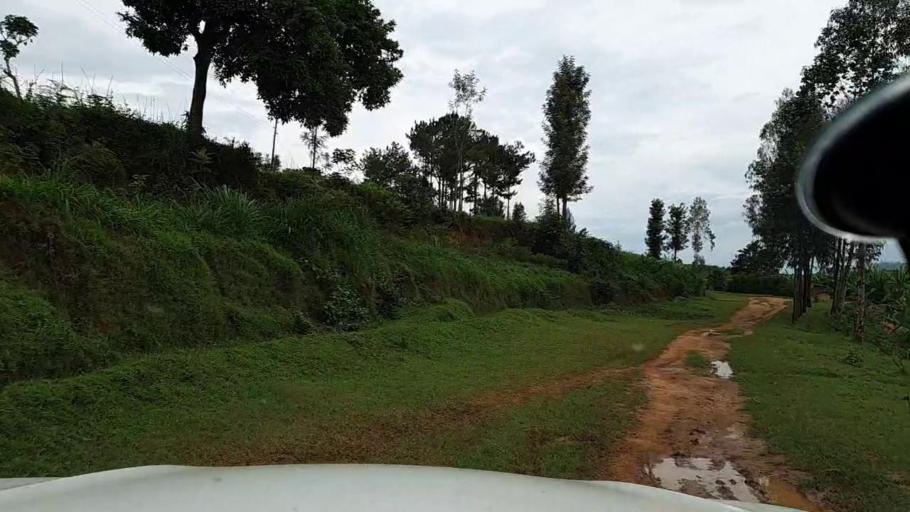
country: RW
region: Southern Province
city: Gitarama
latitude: -2.1168
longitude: 29.6461
